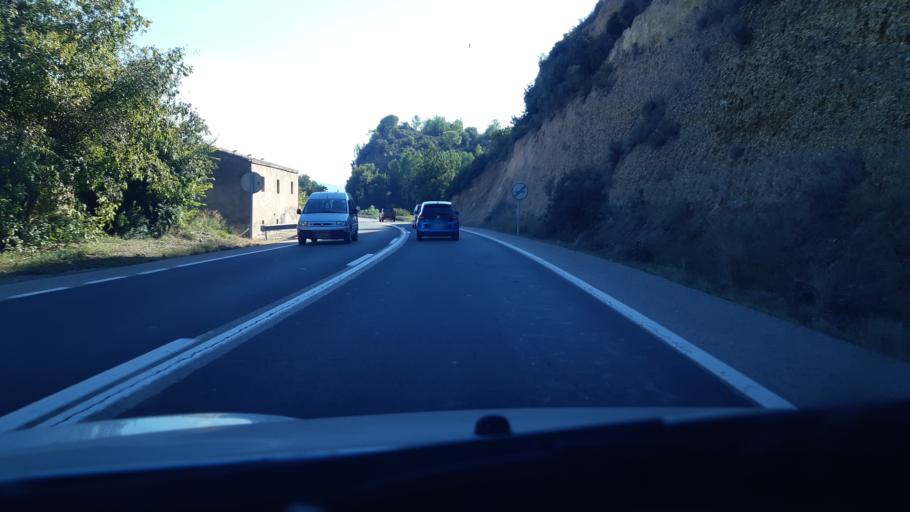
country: ES
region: Catalonia
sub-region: Provincia de Tarragona
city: Tivenys
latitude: 40.8703
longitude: 0.5020
